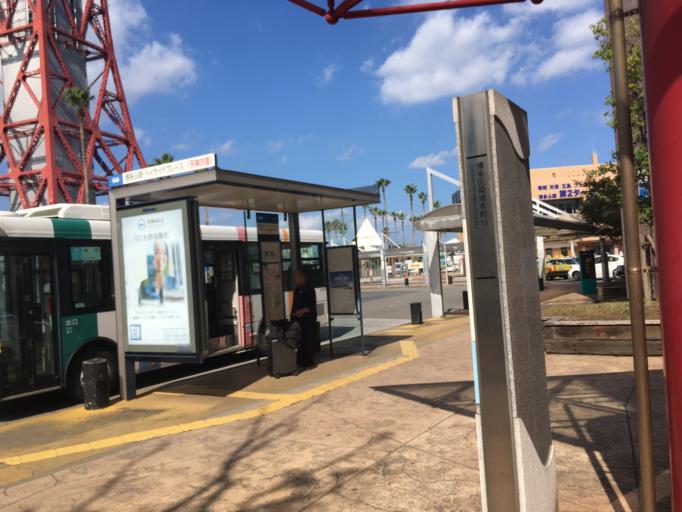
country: JP
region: Fukuoka
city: Fukuoka-shi
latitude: 33.6042
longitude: 130.3985
